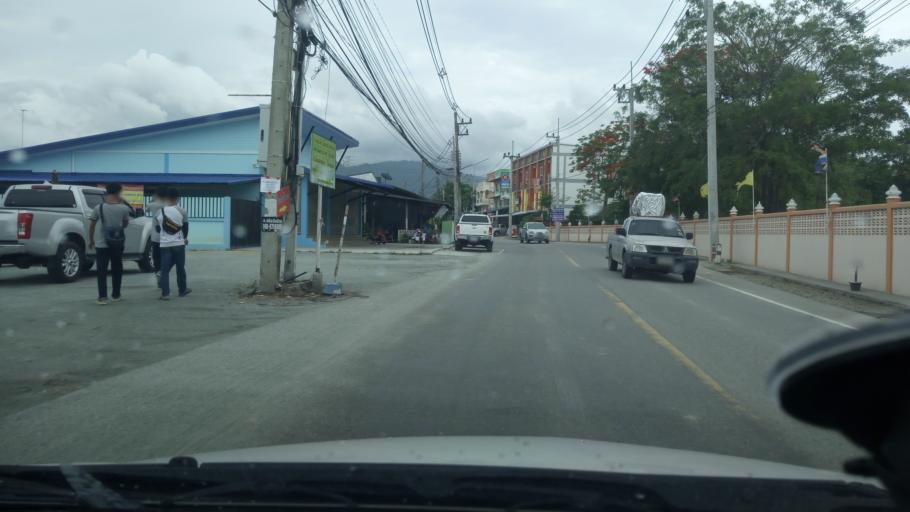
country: TH
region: Chon Buri
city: Ban Bueng
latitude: 13.3406
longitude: 101.0671
